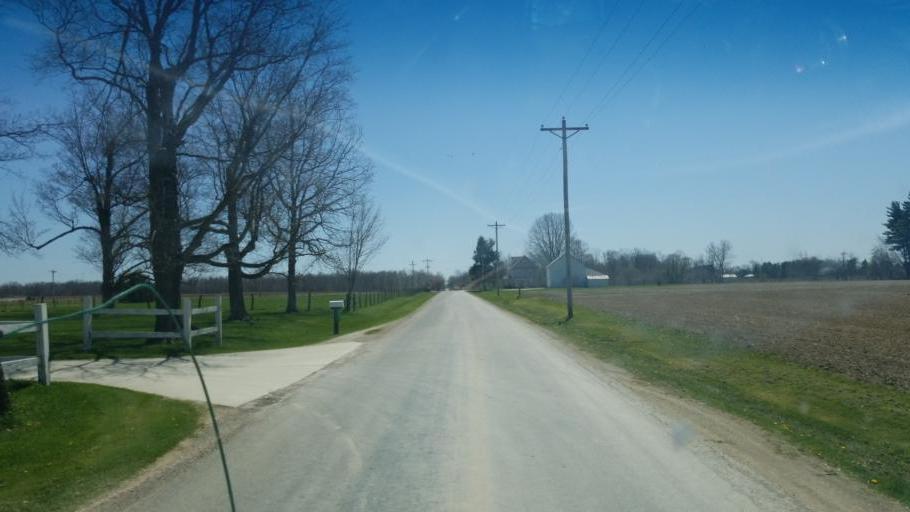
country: US
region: Ohio
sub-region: Huron County
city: Greenwich
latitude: 41.0501
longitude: -82.5115
